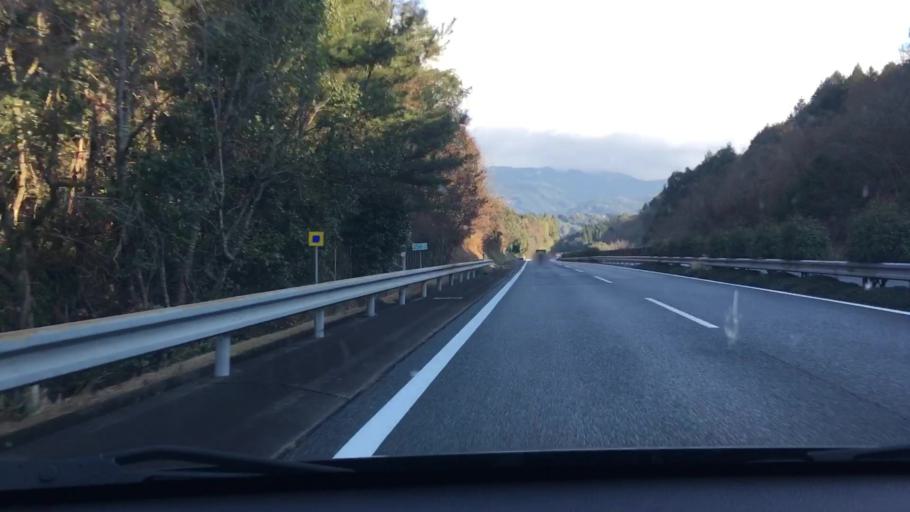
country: JP
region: Kumamoto
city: Hitoyoshi
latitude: 32.1821
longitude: 130.7818
